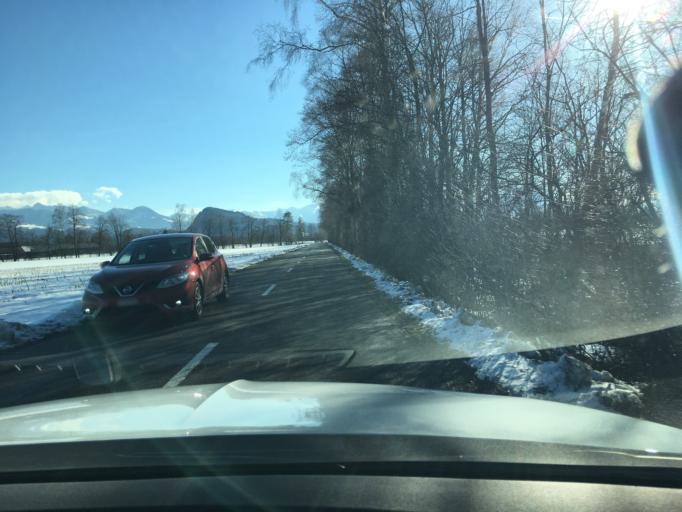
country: CH
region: Saint Gallen
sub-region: Wahlkreis Rheintal
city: Rebstein
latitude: 47.3712
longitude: 9.5919
